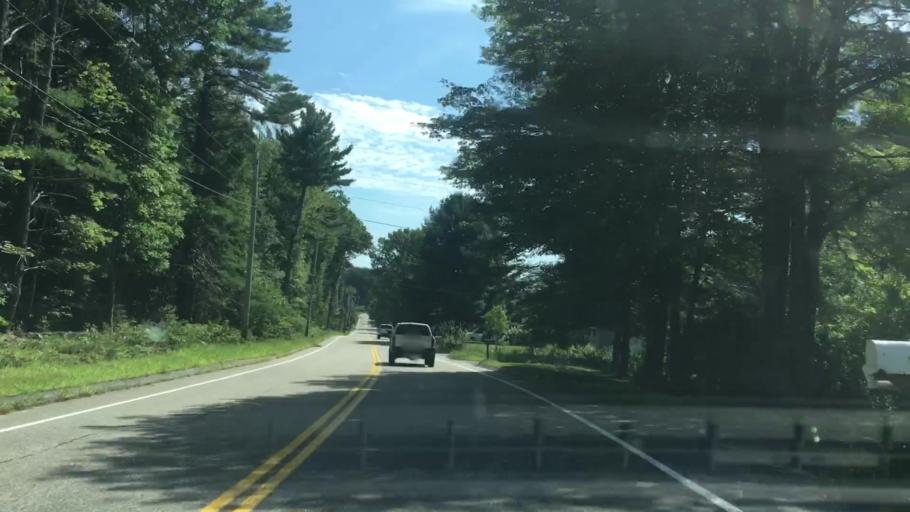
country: US
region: Maine
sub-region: Cumberland County
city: South Portland
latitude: 43.6038
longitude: -70.2672
